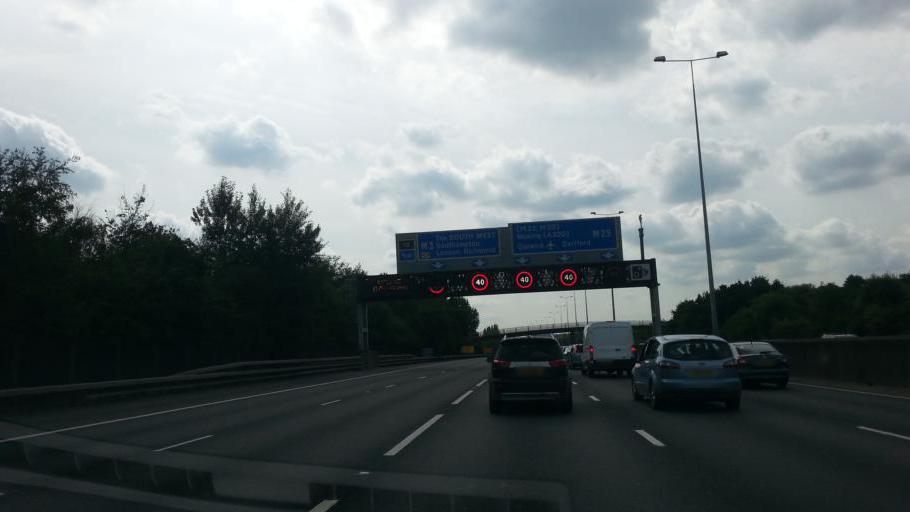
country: GB
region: England
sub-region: Surrey
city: Egham
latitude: 51.4160
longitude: -0.5398
